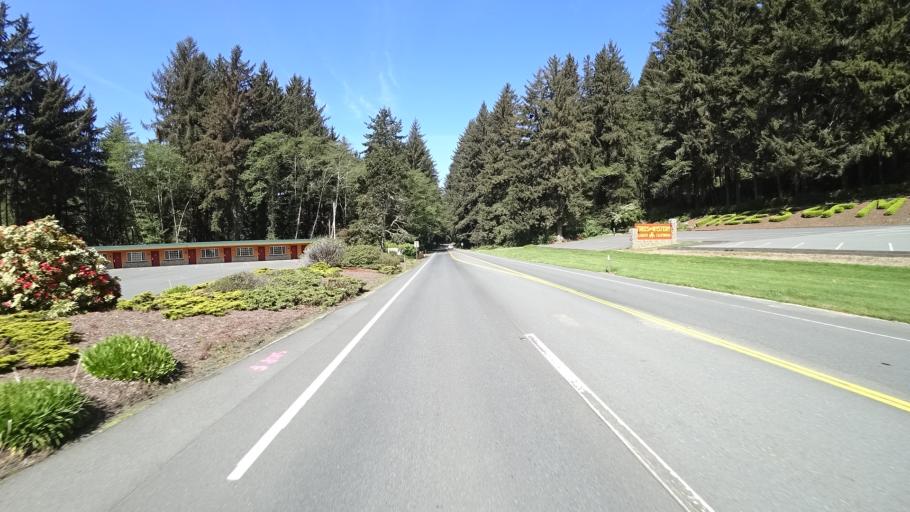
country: US
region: California
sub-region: Del Norte County
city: Bertsch-Oceanview
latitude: 41.5841
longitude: -124.0871
